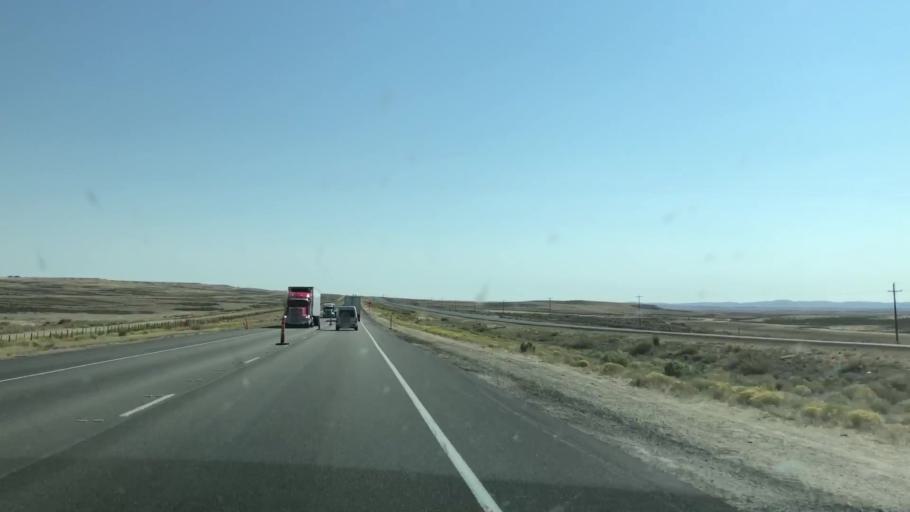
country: US
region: Wyoming
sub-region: Carbon County
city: Rawlins
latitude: 41.7456
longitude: -107.6162
